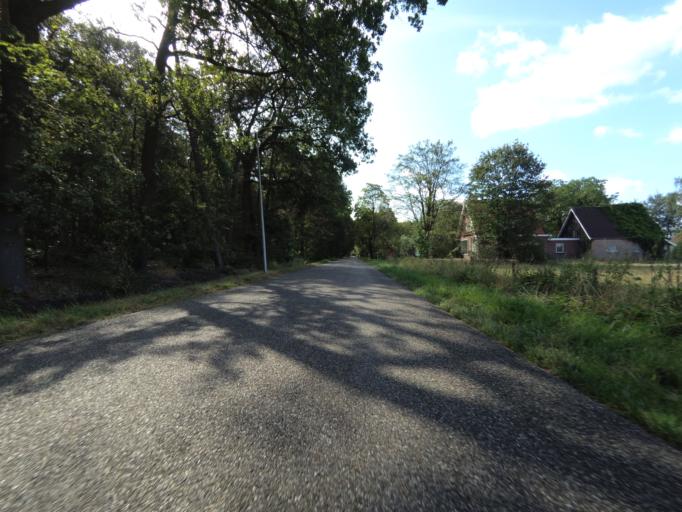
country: NL
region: Overijssel
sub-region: Gemeente Haaksbergen
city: Haaksbergen
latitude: 52.1927
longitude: 6.7982
